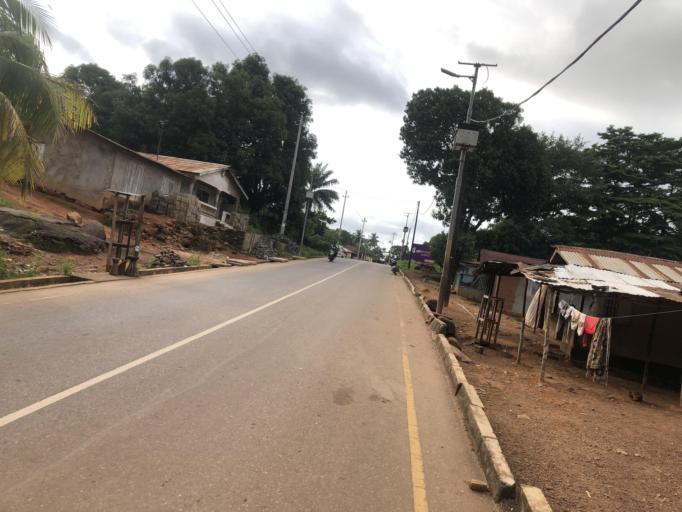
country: SL
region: Northern Province
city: Port Loko
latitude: 8.7597
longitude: -12.7860
